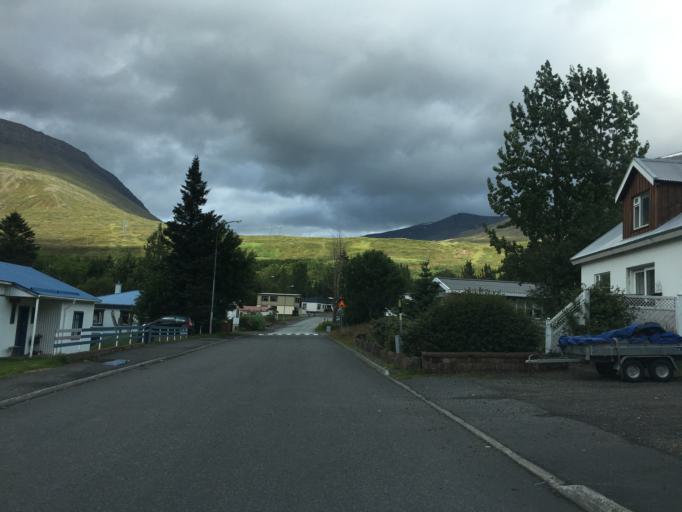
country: IS
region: East
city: Reydarfjoerdur
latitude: 65.0337
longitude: -14.2166
